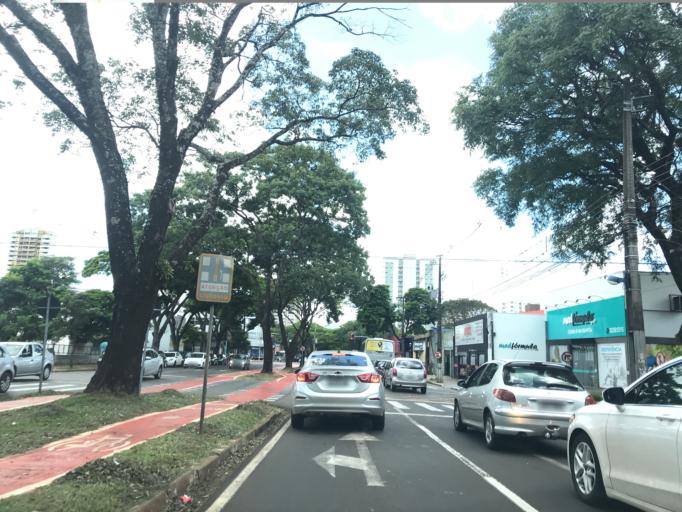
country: BR
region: Parana
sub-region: Maringa
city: Maringa
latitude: -23.4136
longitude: -51.9255
